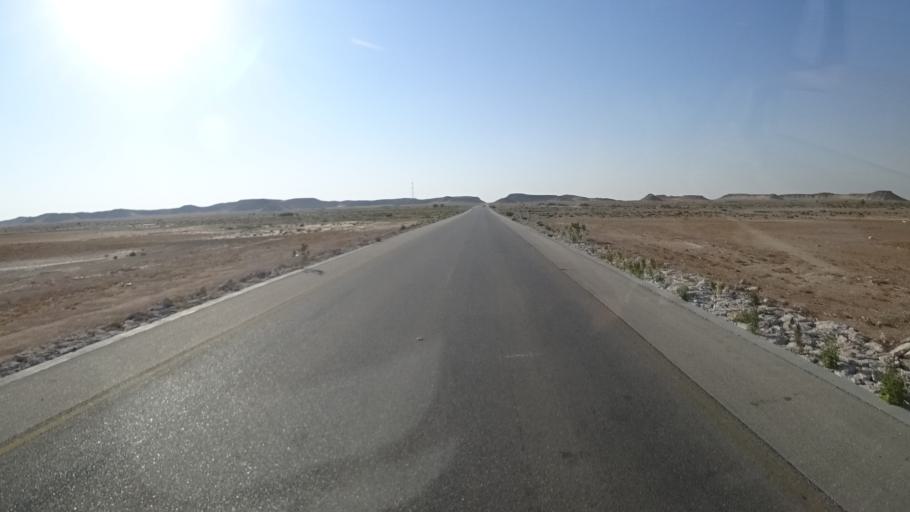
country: OM
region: Zufar
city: Salalah
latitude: 17.6401
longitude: 53.8678
